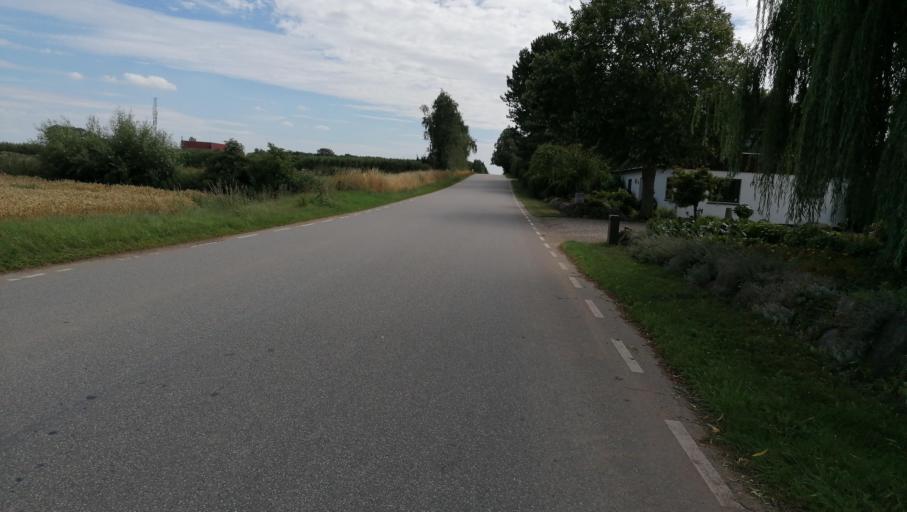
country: DK
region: Zealand
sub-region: Odsherred Kommune
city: Horve
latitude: 55.7618
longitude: 11.4391
